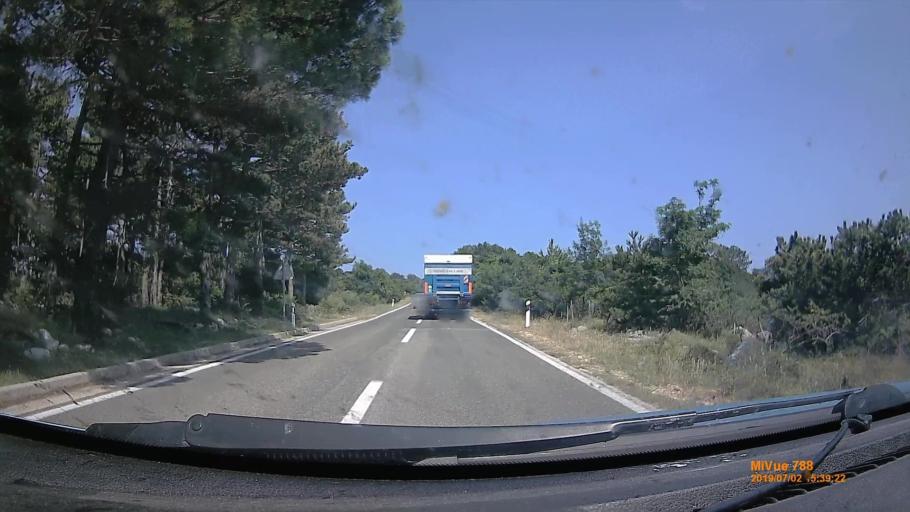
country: HR
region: Primorsko-Goranska
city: Cres
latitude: 44.9711
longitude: 14.4249
